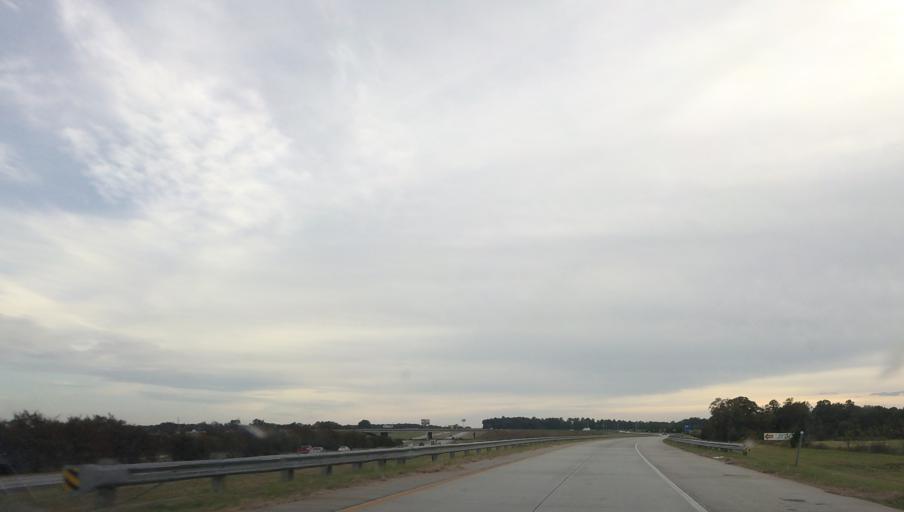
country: US
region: Georgia
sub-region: Peach County
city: Byron
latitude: 32.5908
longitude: -83.7436
